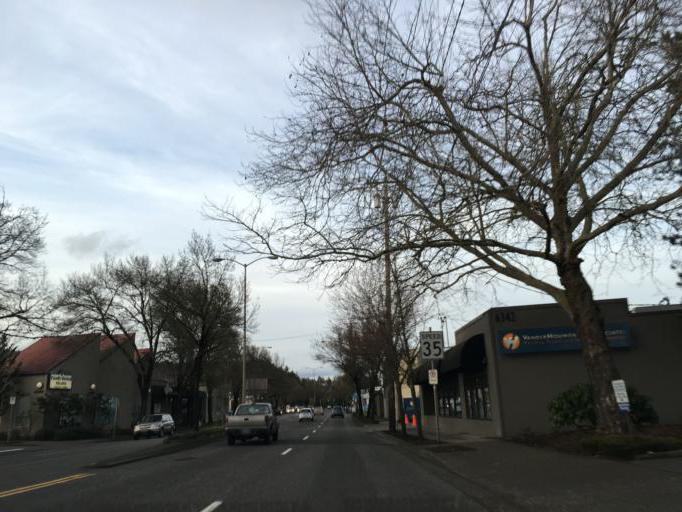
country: US
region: Oregon
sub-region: Clackamas County
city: Milwaukie
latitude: 45.4777
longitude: -122.6722
